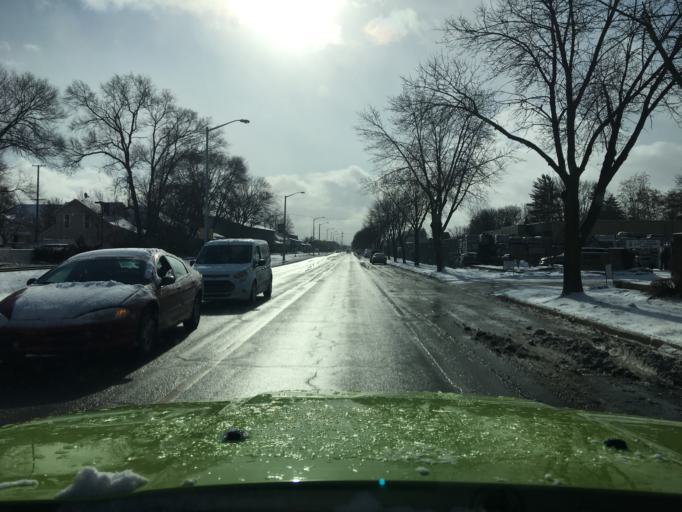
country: US
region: Michigan
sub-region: Kent County
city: Grand Rapids
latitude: 42.9847
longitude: -85.6831
